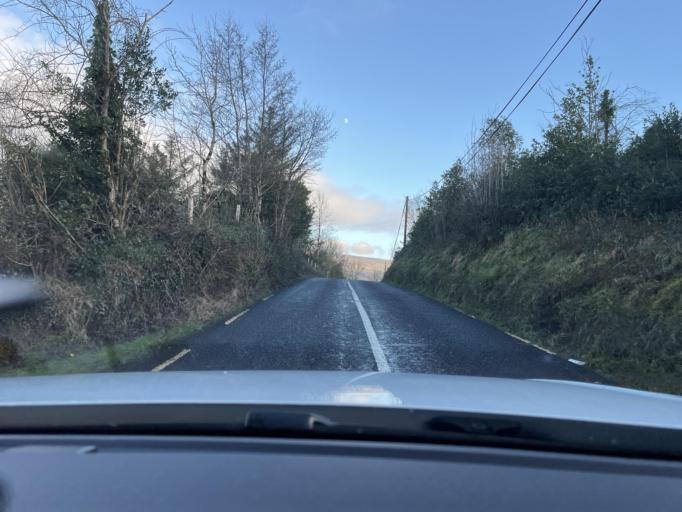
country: IE
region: Connaught
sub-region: County Leitrim
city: Manorhamilton
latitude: 54.1918
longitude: -7.9175
